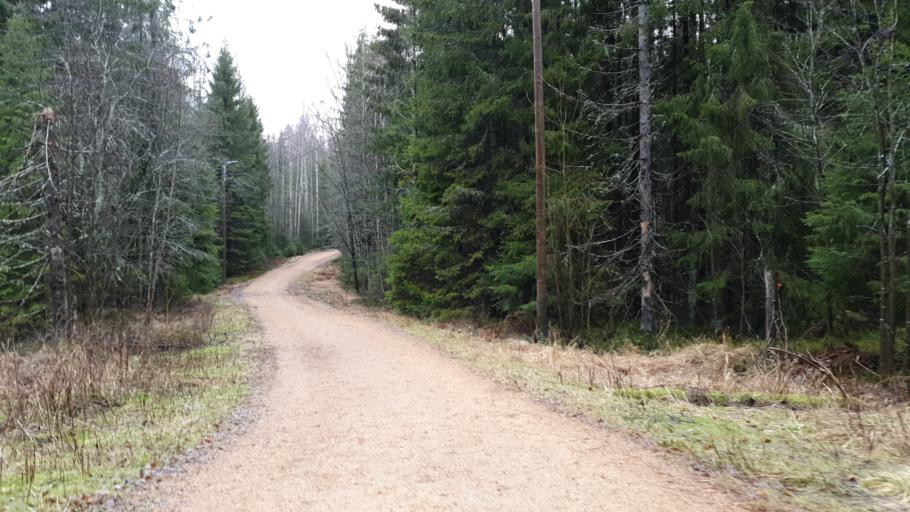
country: FI
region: Uusimaa
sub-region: Helsinki
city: Helsinki
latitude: 60.2617
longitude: 24.9137
